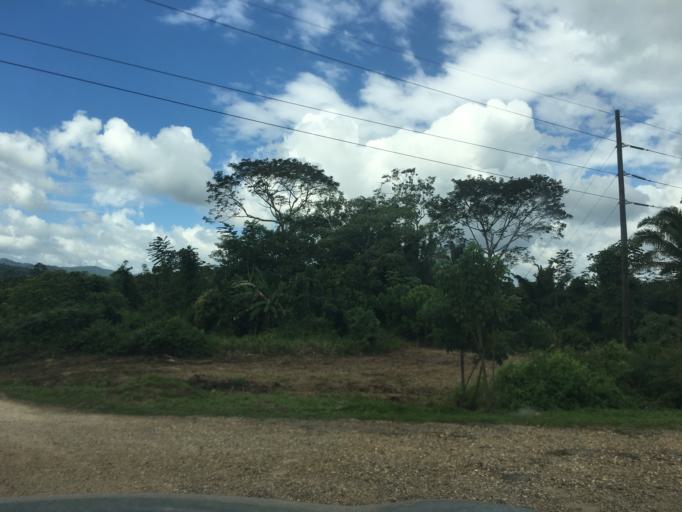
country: BZ
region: Stann Creek
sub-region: Dangriga
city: Dangriga
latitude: 16.9187
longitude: -88.3432
